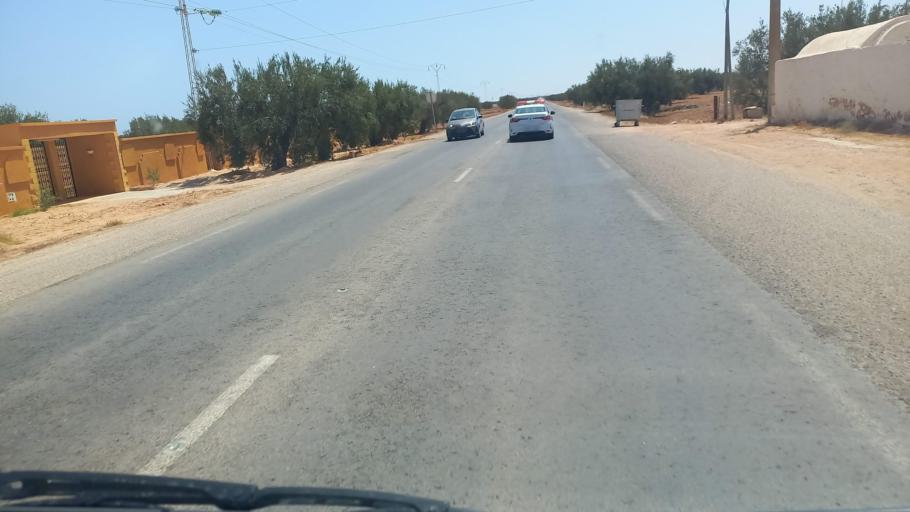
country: TN
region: Madanin
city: Zarzis
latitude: 33.5730
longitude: 11.0400
